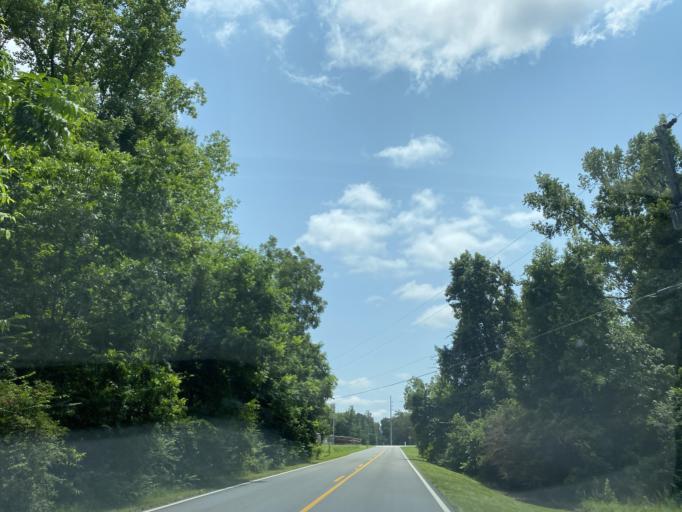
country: US
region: Georgia
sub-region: Telfair County
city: Lumber City
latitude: 31.9387
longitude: -82.6870
